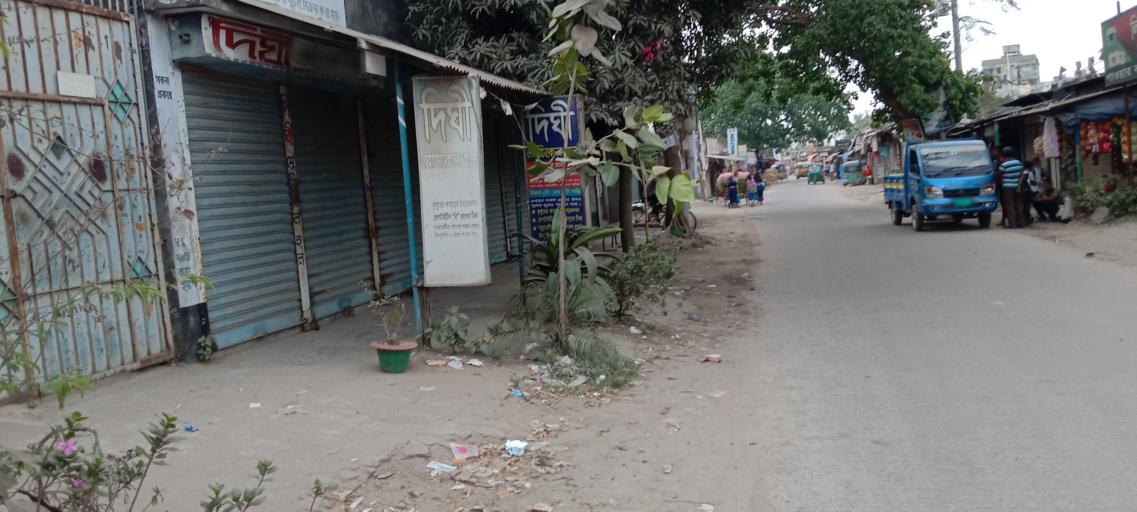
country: BD
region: Dhaka
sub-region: Dhaka
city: Dhaka
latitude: 23.6589
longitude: 90.4148
